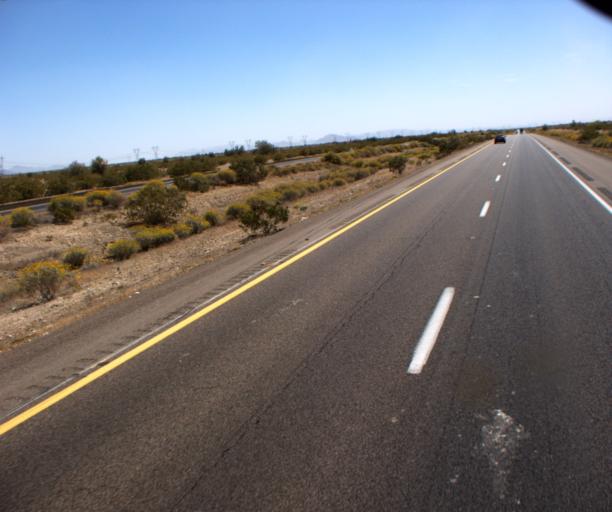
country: US
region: Arizona
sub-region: Maricopa County
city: Gila Bend
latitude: 33.0706
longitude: -112.6462
